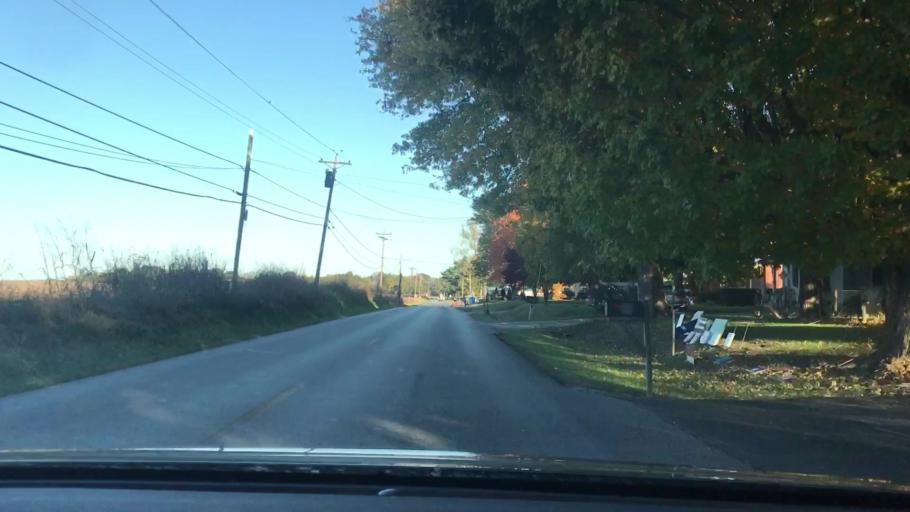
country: US
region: Kentucky
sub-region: Simpson County
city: Franklin
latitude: 36.7397
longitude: -86.5860
